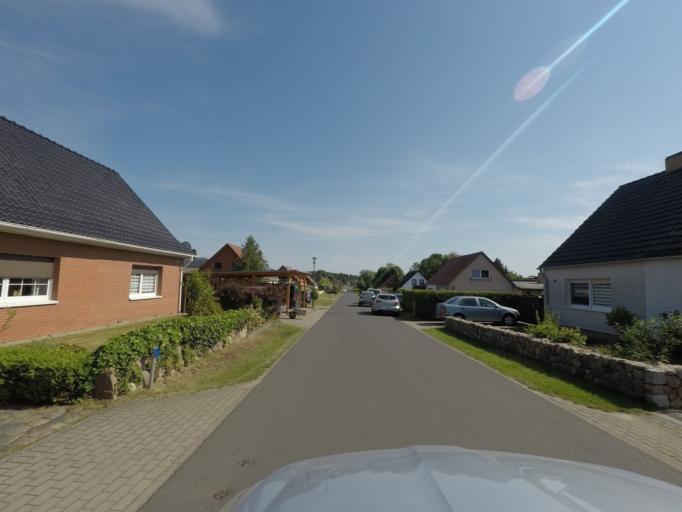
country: DE
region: Brandenburg
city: Melchow
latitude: 52.8659
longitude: 13.7216
